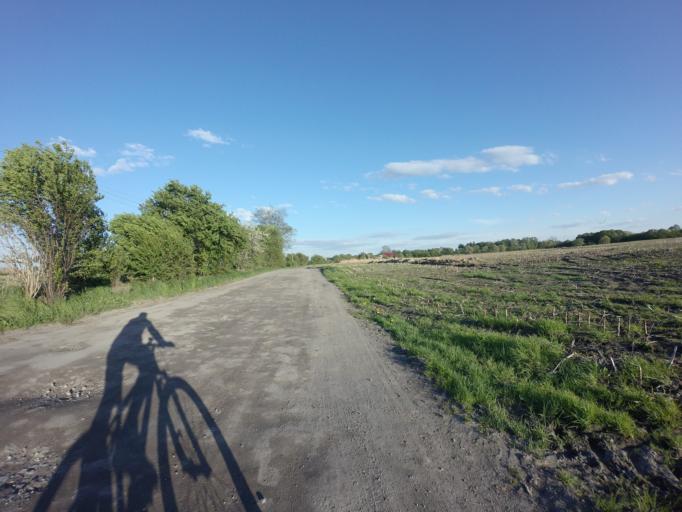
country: PL
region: West Pomeranian Voivodeship
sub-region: Powiat choszczenski
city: Choszczno
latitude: 53.1375
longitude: 15.4367
